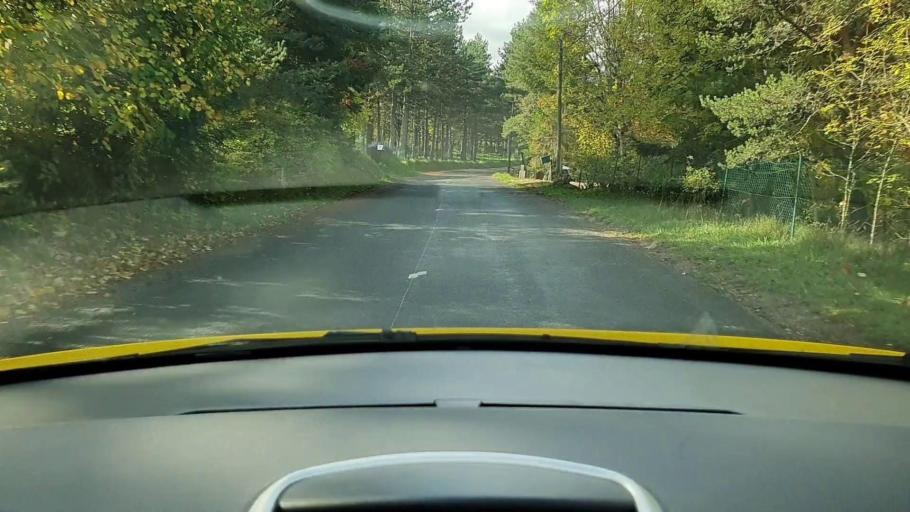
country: FR
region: Languedoc-Roussillon
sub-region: Departement de la Lozere
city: Meyrueis
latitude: 44.1126
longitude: 3.4699
